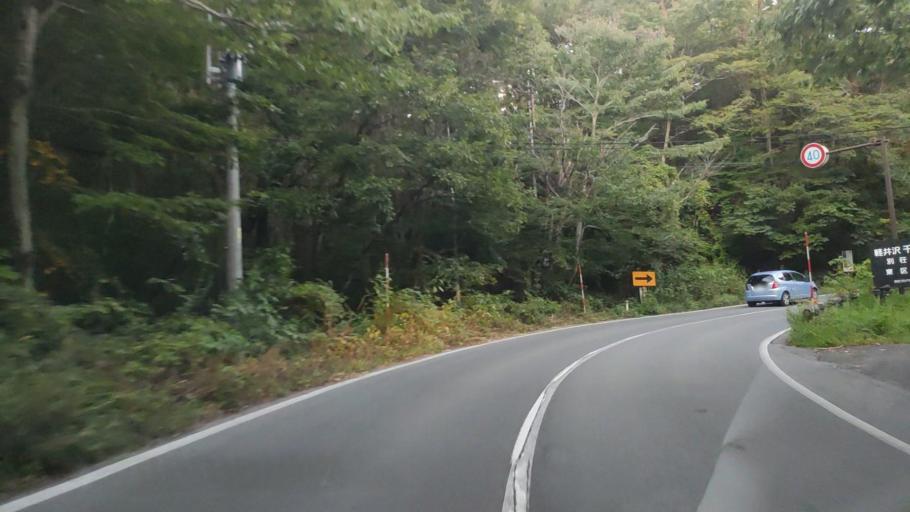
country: JP
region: Nagano
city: Komoro
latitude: 36.3818
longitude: 138.5911
